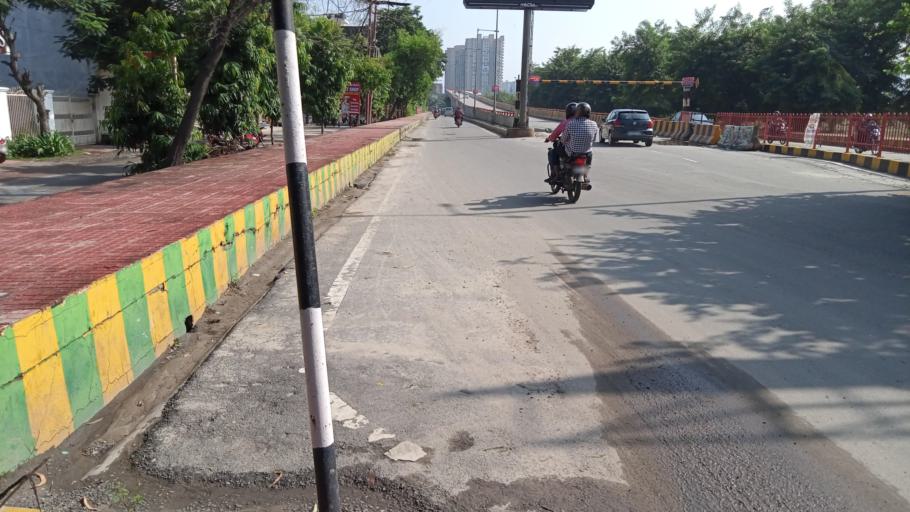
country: IN
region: Uttar Pradesh
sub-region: Ghaziabad
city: Ghaziabad
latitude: 28.6618
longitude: 77.3739
